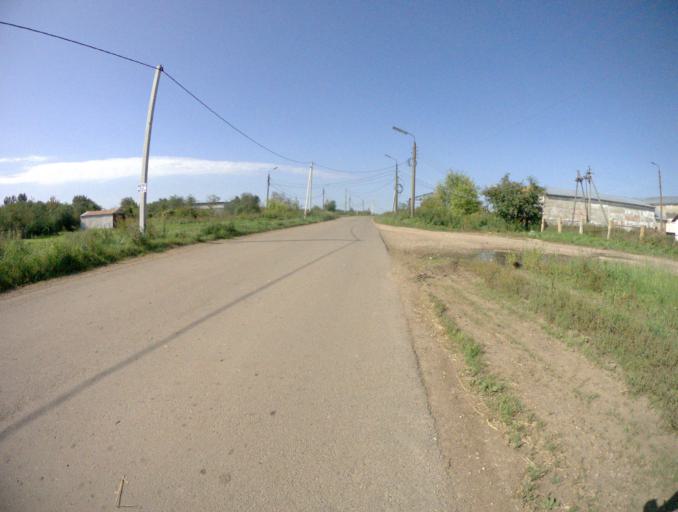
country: RU
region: Vladimir
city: Bogolyubovo
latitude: 56.2127
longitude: 40.5091
